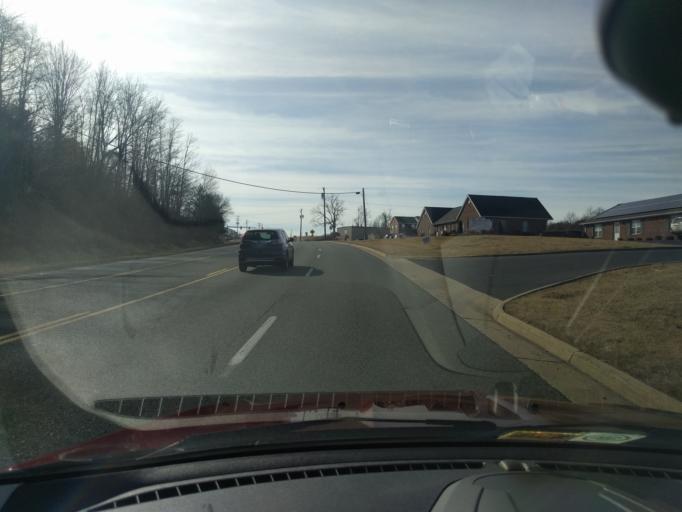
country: US
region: Virginia
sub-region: Augusta County
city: Verona
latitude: 38.2072
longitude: -79.0038
